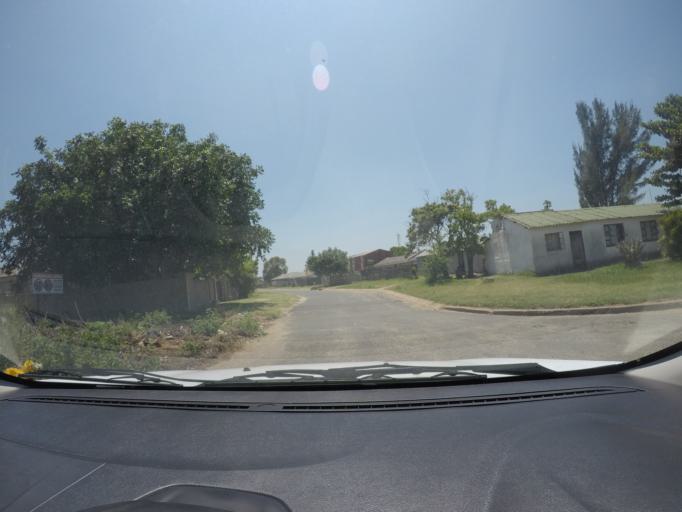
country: ZA
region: KwaZulu-Natal
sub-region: uThungulu District Municipality
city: eSikhawini
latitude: -28.8770
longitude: 31.9111
